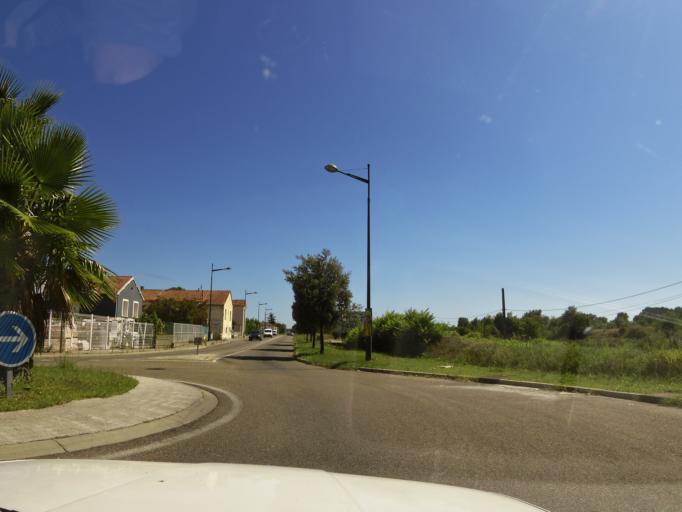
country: FR
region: Languedoc-Roussillon
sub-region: Departement du Gard
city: Saint-Hilaire-de-Brethmas
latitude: 44.1030
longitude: 4.1037
